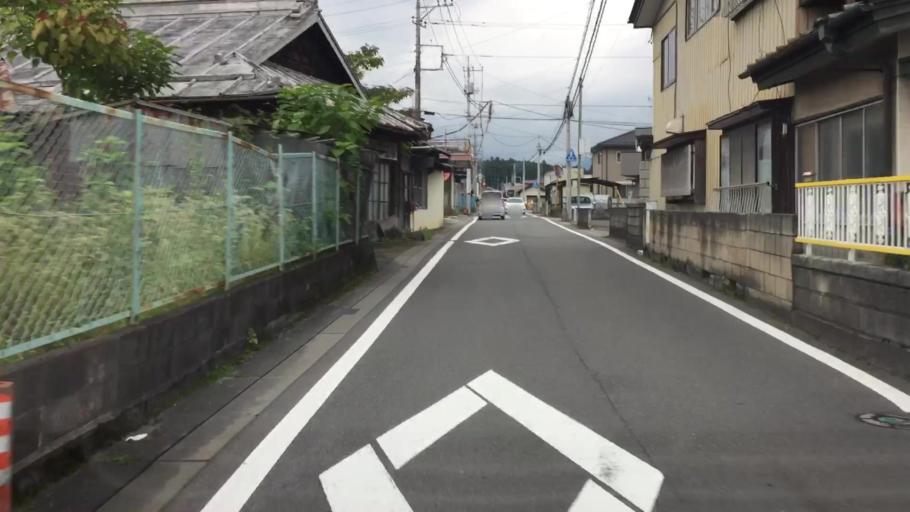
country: JP
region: Tochigi
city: Imaichi
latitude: 36.7344
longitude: 139.6874
